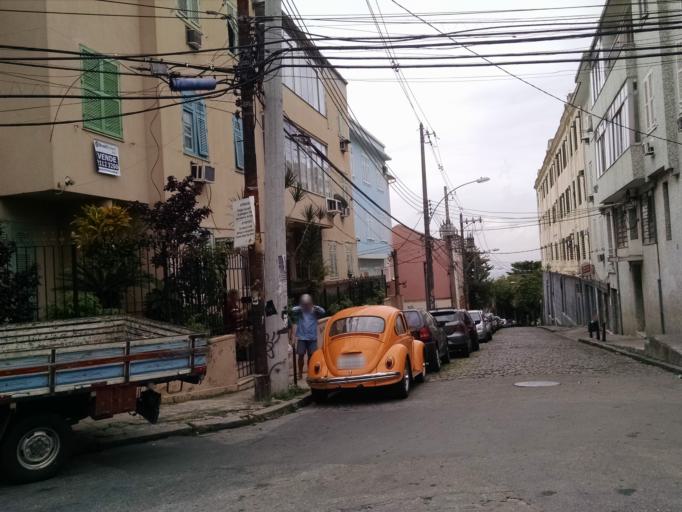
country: BR
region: Rio de Janeiro
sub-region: Rio De Janeiro
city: Rio de Janeiro
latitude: -22.9251
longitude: -43.1898
